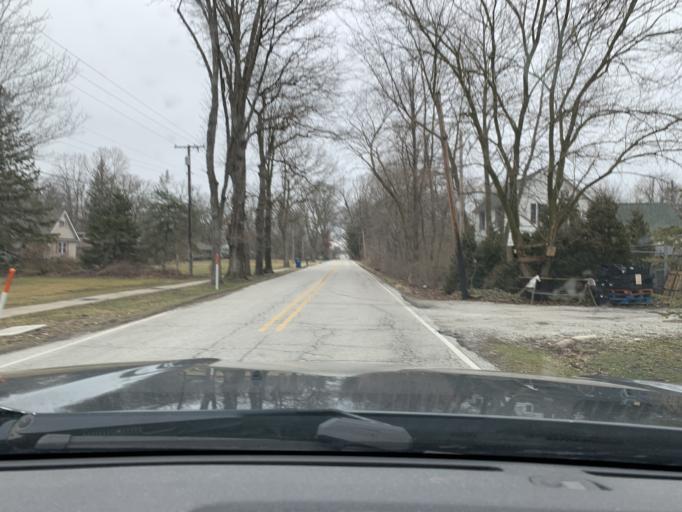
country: US
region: Indiana
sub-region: Porter County
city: Chesterton
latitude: 41.6170
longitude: -87.0287
